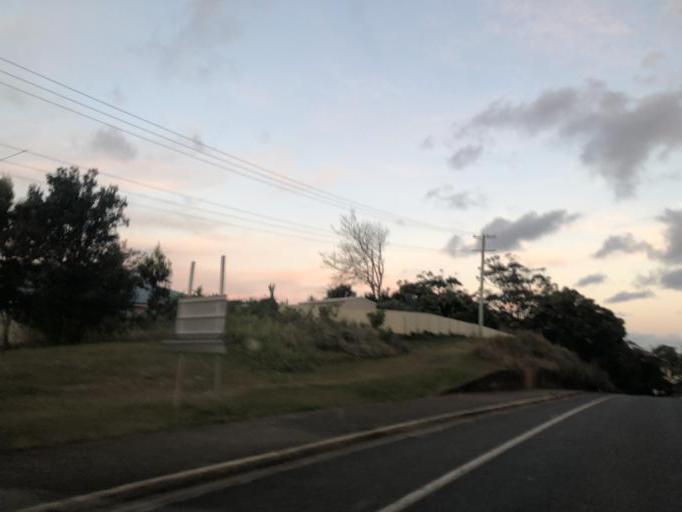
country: AU
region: New South Wales
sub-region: Coffs Harbour
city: Woolgoolga
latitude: -30.1074
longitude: 153.1893
